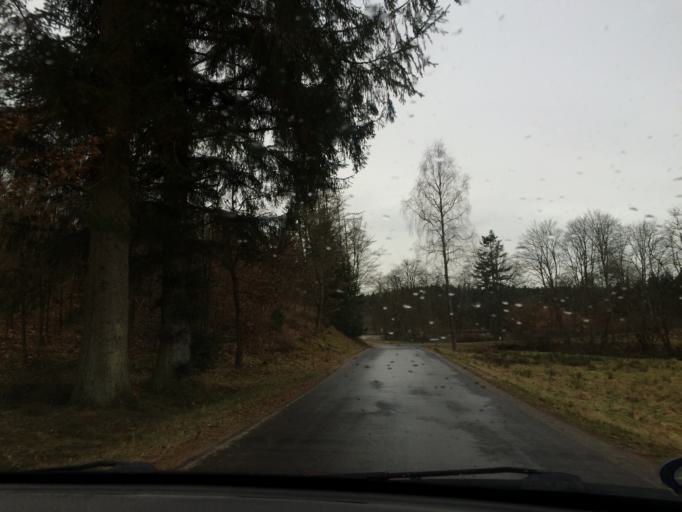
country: DK
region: Central Jutland
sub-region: Silkeborg Kommune
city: Virklund
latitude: 56.0317
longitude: 9.4927
